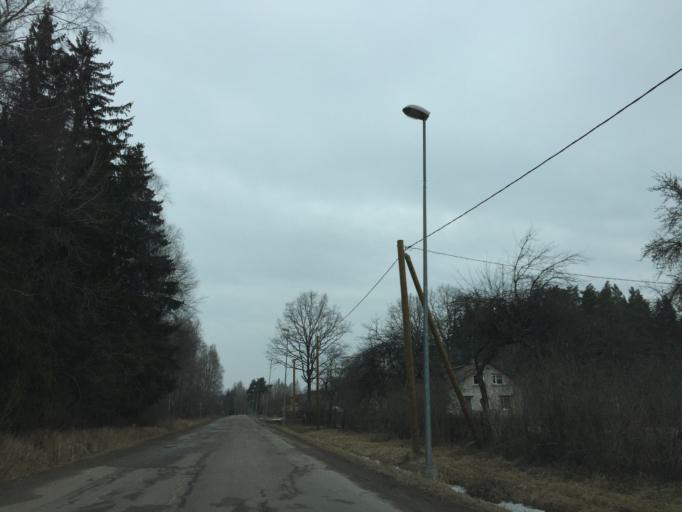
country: LV
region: Ozolnieku
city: Ozolnieki
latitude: 56.7161
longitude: 23.8348
